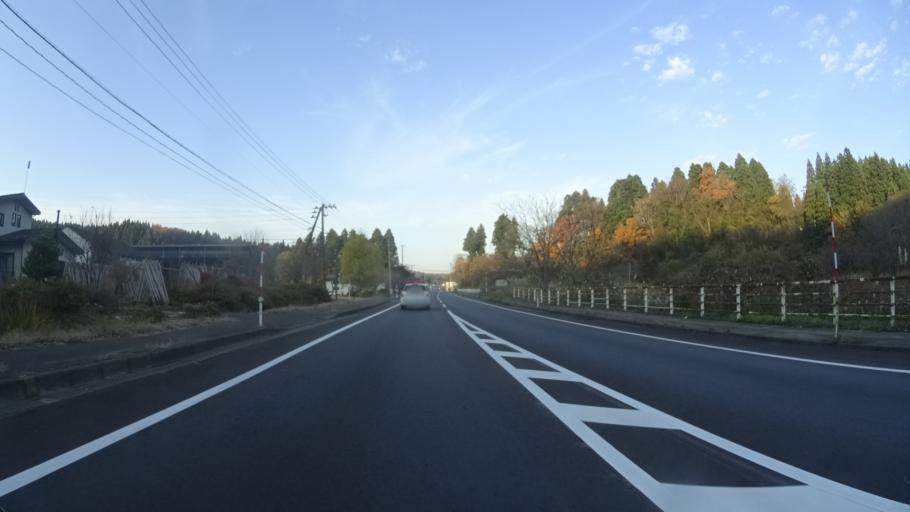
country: JP
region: Niigata
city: Nagaoka
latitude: 37.4271
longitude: 138.7261
